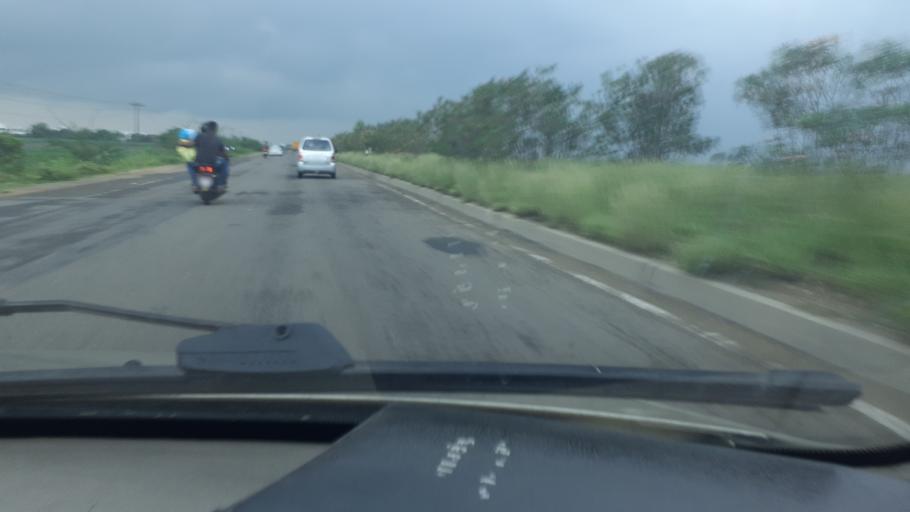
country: IN
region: Tamil Nadu
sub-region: Thoothukkudi
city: Kovilpatti
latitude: 9.1253
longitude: 77.8209
